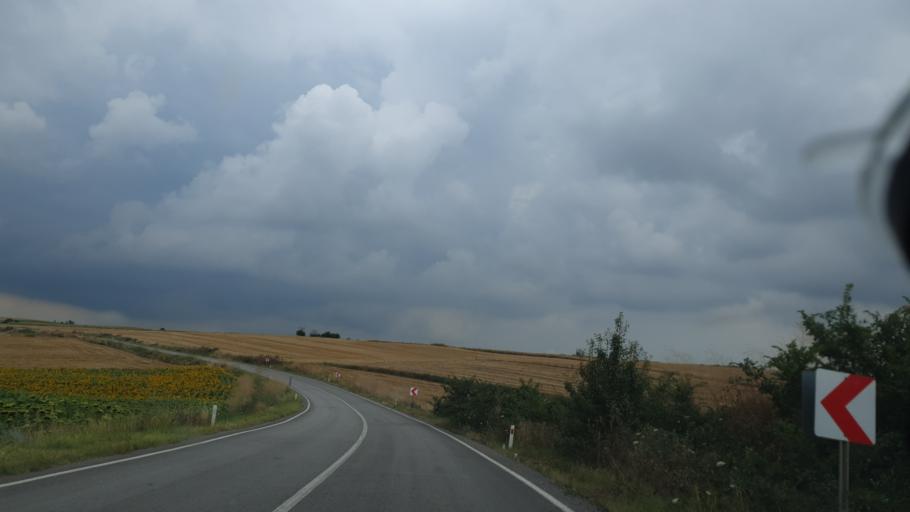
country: TR
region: Tekirdag
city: Hayrabolu
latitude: 41.2284
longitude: 27.0361
